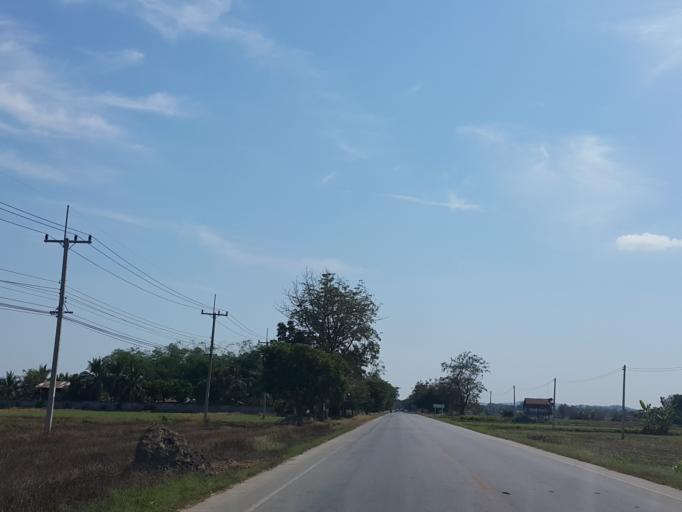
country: TH
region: Sukhothai
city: Thung Saliam
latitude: 17.3394
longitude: 99.6069
